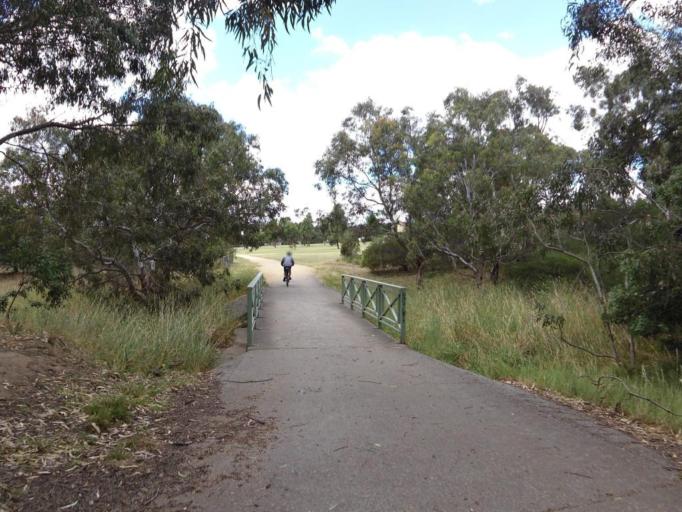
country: AU
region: Victoria
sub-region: Hume
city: Westmeadows
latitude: -37.6742
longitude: 144.8745
